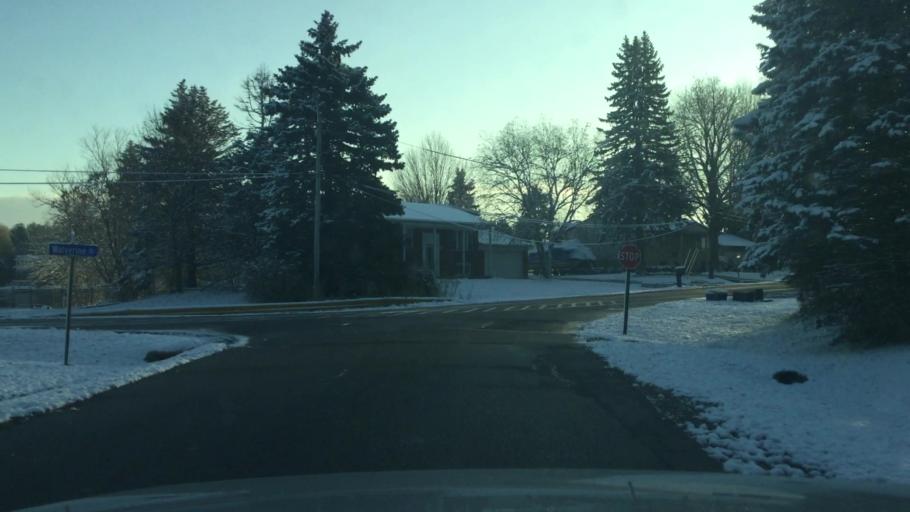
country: US
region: Michigan
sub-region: Oakland County
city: Walled Lake
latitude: 42.5473
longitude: -83.4851
